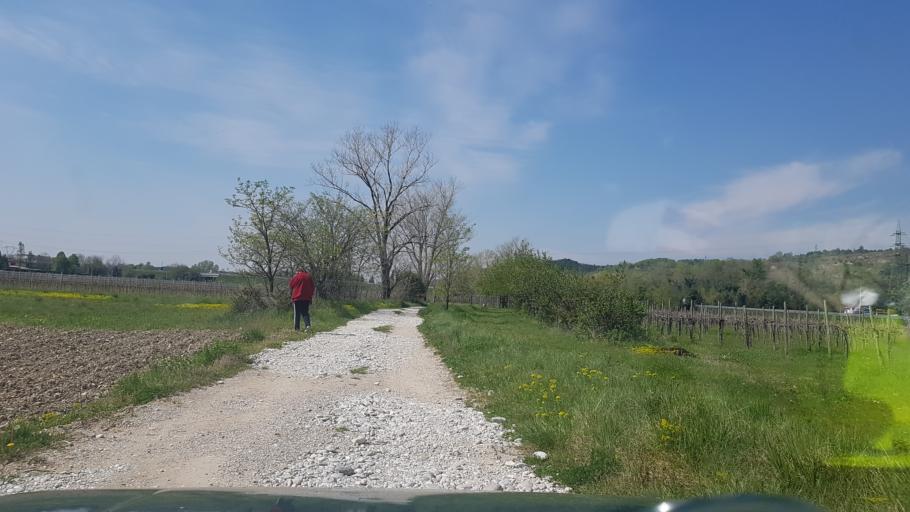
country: IT
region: Friuli Venezia Giulia
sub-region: Provincia di Gorizia
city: Ronchi dei Legionari
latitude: 45.8400
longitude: 13.4991
